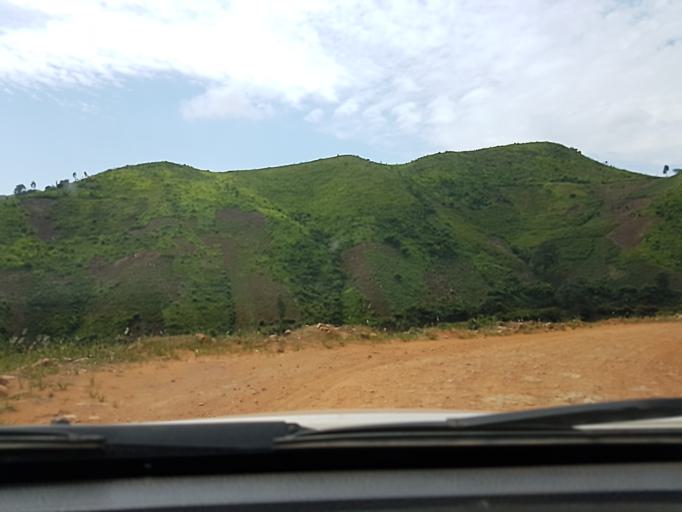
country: RW
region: Western Province
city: Cyangugu
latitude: -2.7064
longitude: 28.9451
